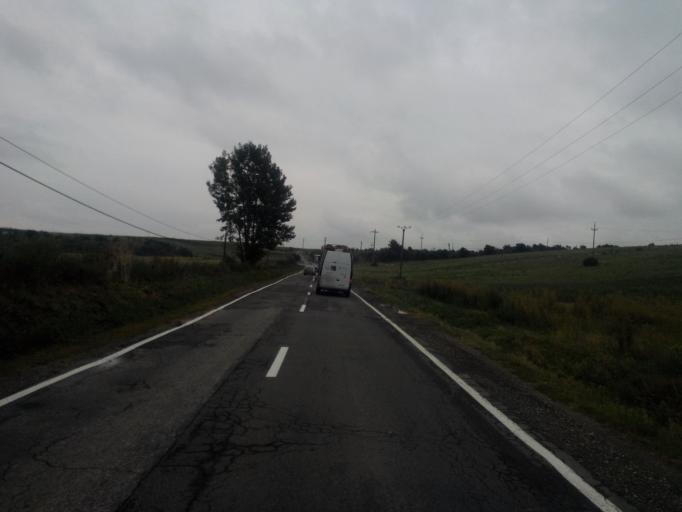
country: RO
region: Cluj
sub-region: Comuna Moldovenesti
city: Moldovenesti
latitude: 46.5091
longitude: 23.6684
